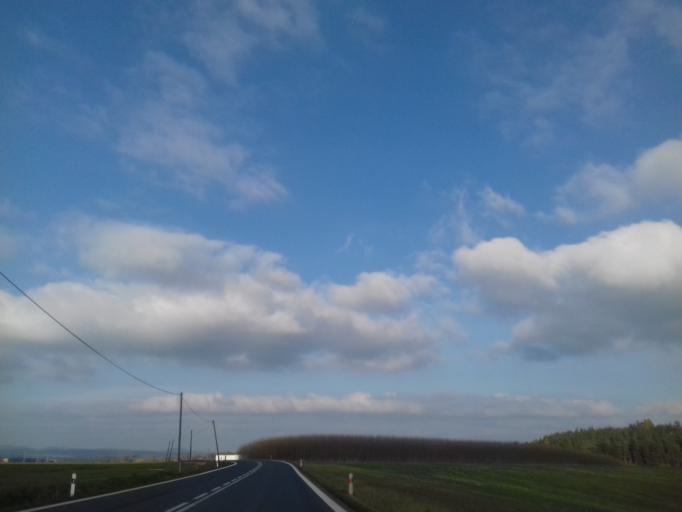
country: CZ
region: Plzensky
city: Meclov
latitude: 49.4916
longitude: 12.8815
